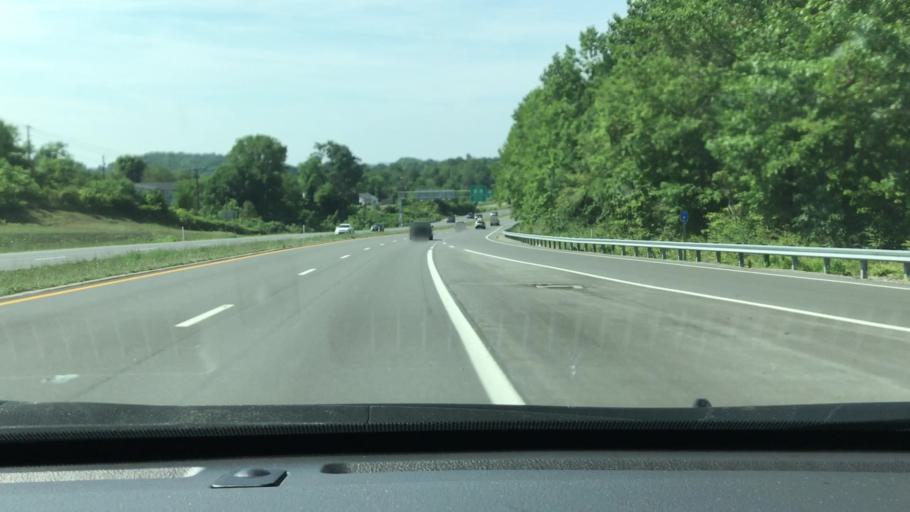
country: US
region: West Virginia
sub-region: Fayette County
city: Oak Hill
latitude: 37.9637
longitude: -81.1473
